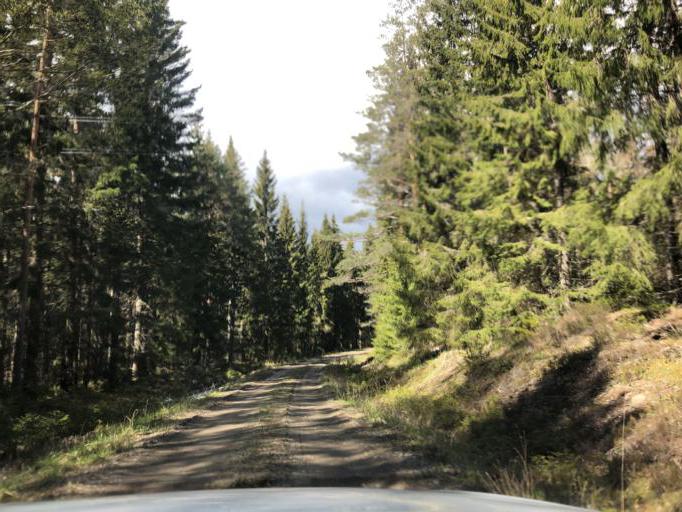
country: SE
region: Dalarna
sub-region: Avesta Kommun
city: Horndal
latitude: 60.2327
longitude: 16.6014
